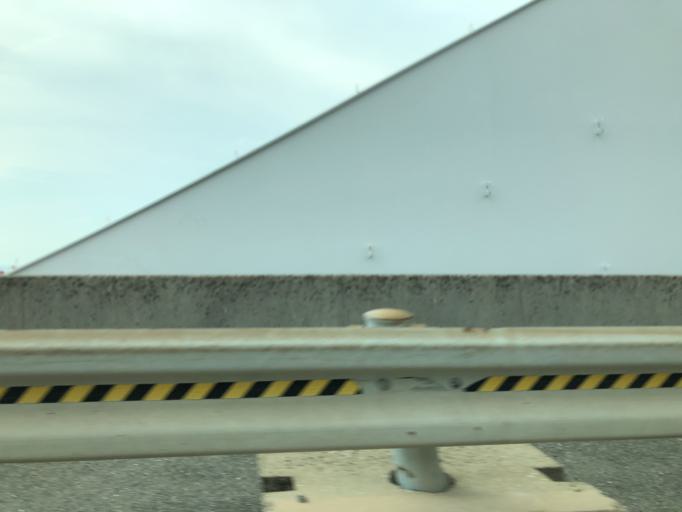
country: JP
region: Hyogo
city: Ashiya
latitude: 34.7000
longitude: 135.2734
